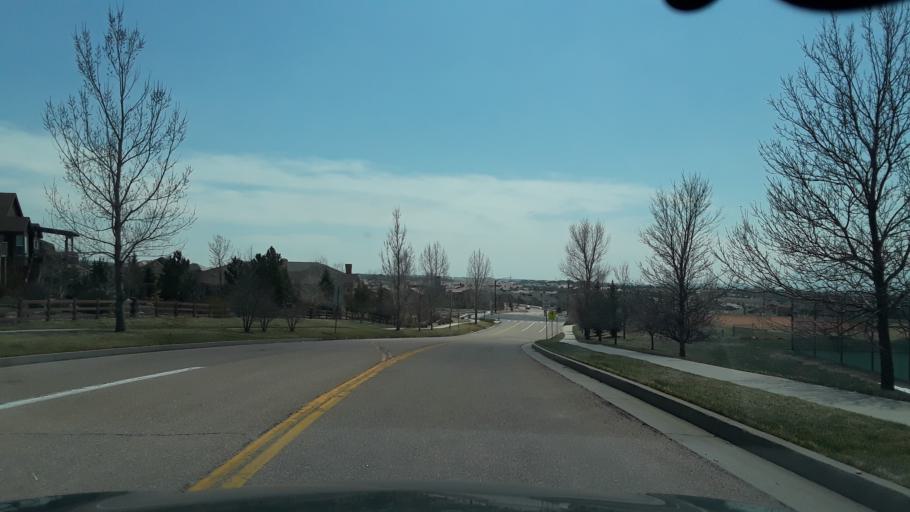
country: US
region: Colorado
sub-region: El Paso County
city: Gleneagle
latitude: 39.0319
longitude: -104.7905
